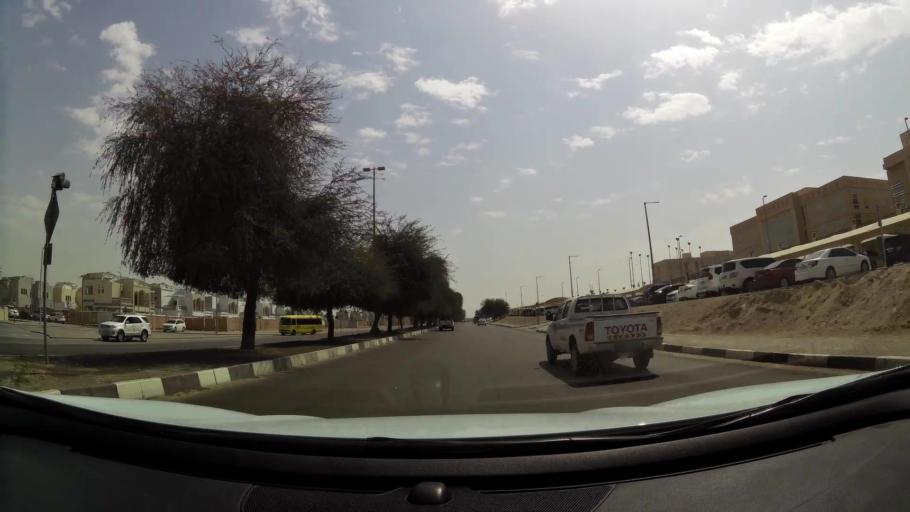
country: AE
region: Abu Dhabi
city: Abu Dhabi
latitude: 24.3062
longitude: 54.6196
